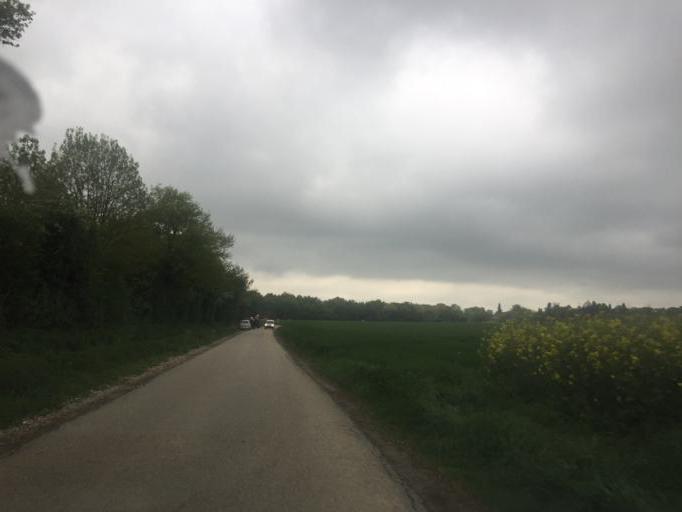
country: FR
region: Rhone-Alpes
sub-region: Departement de l'Ain
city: Tramoyes
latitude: 45.8877
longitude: 4.9736
